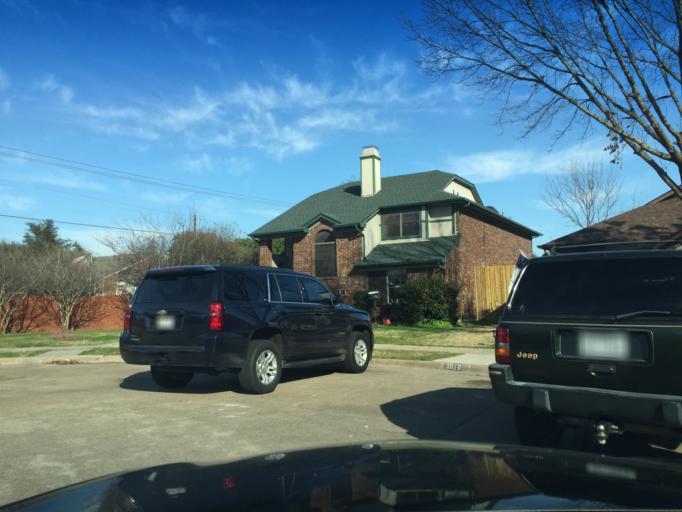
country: US
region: Texas
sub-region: Dallas County
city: Carrollton
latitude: 32.9984
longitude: -96.8974
